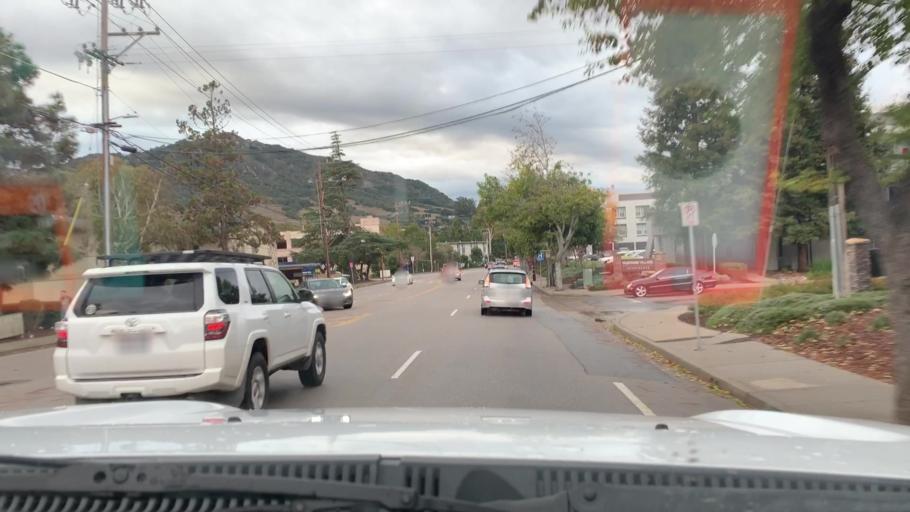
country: US
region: California
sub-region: San Luis Obispo County
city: San Luis Obispo
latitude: 35.2949
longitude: -120.6645
